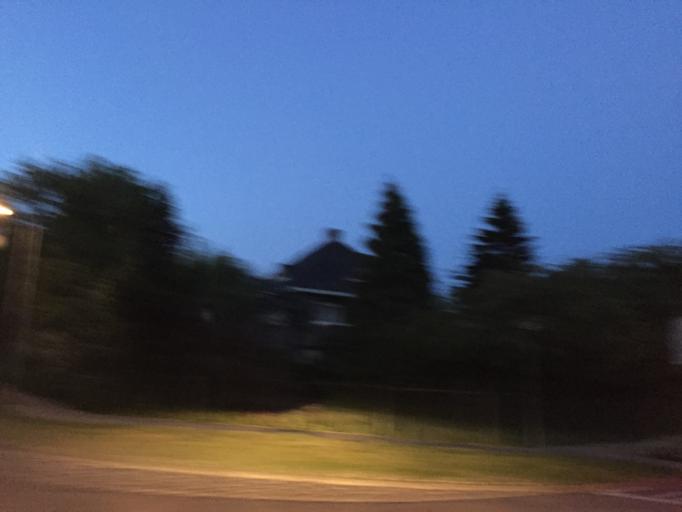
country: NL
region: South Holland
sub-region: Gemeente Waddinxveen
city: Groenswaard
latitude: 52.0447
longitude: 4.6406
